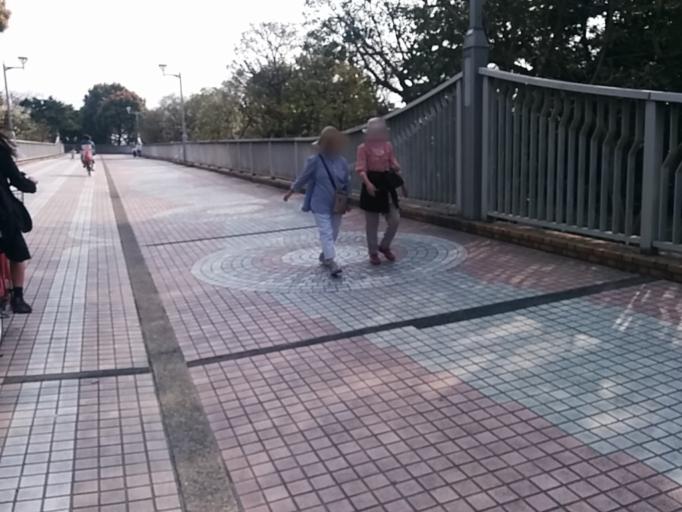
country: JP
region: Tokyo
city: Urayasu
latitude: 35.6480
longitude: 139.8562
